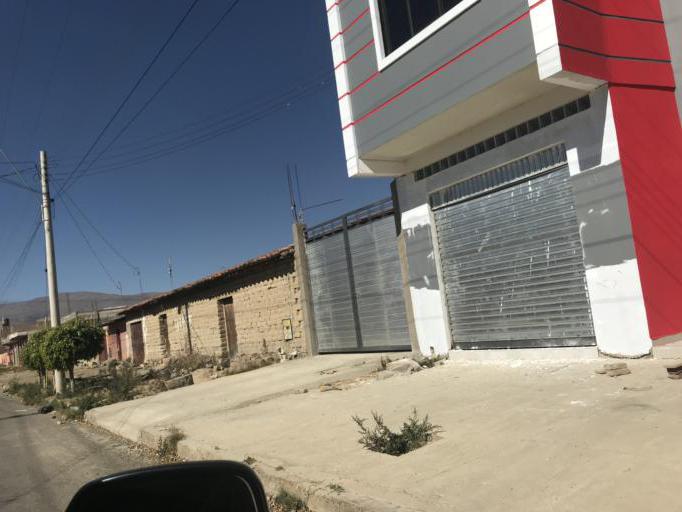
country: BO
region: Cochabamba
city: Punata
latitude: -17.5510
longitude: -65.8490
